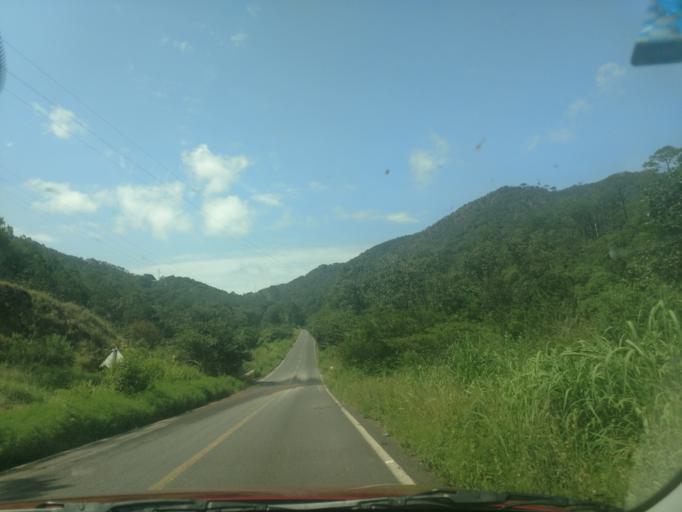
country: MX
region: Jalisco
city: Talpa de Allende
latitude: 20.4331
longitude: -104.7931
